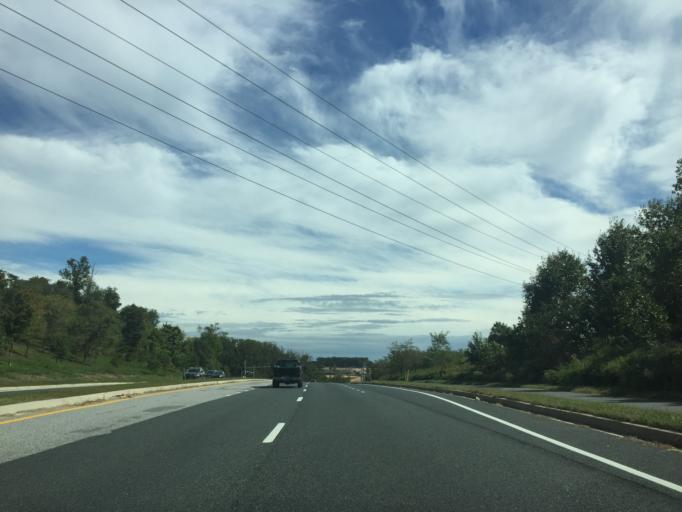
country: US
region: Maryland
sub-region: Baltimore County
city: White Marsh
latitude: 39.3613
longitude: -76.4189
